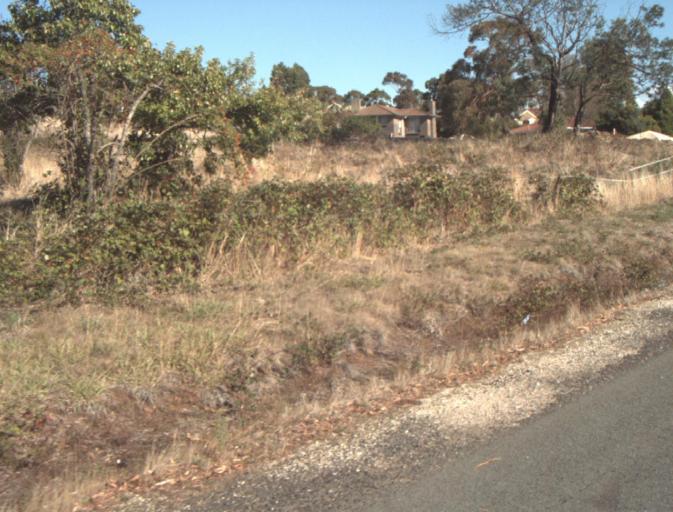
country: AU
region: Tasmania
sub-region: Launceston
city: Mayfield
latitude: -41.3721
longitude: 147.1378
